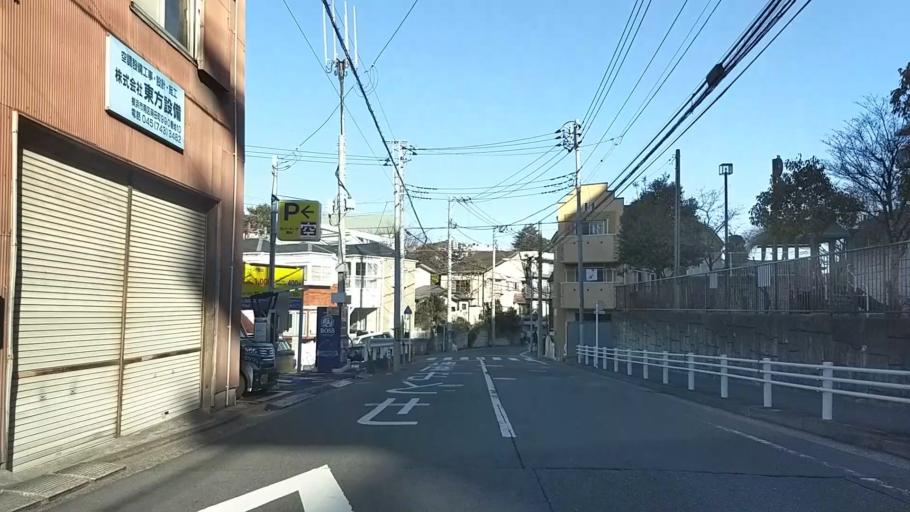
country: JP
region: Kanagawa
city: Yokohama
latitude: 35.4237
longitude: 139.6115
